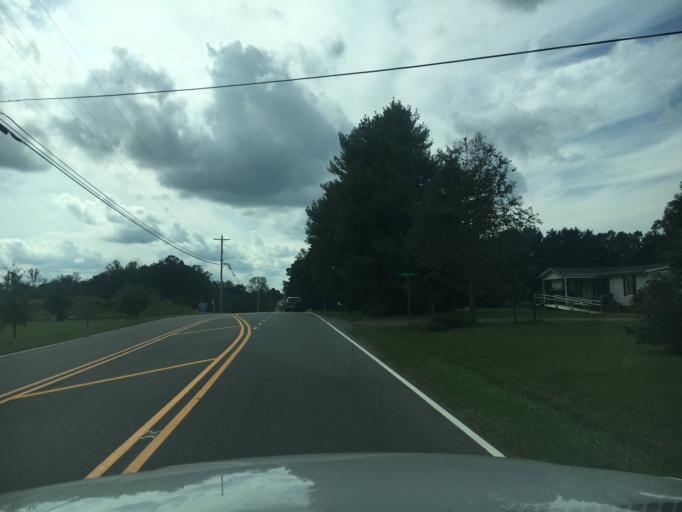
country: US
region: North Carolina
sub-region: Gaston County
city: Dallas
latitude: 35.3109
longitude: -81.2086
